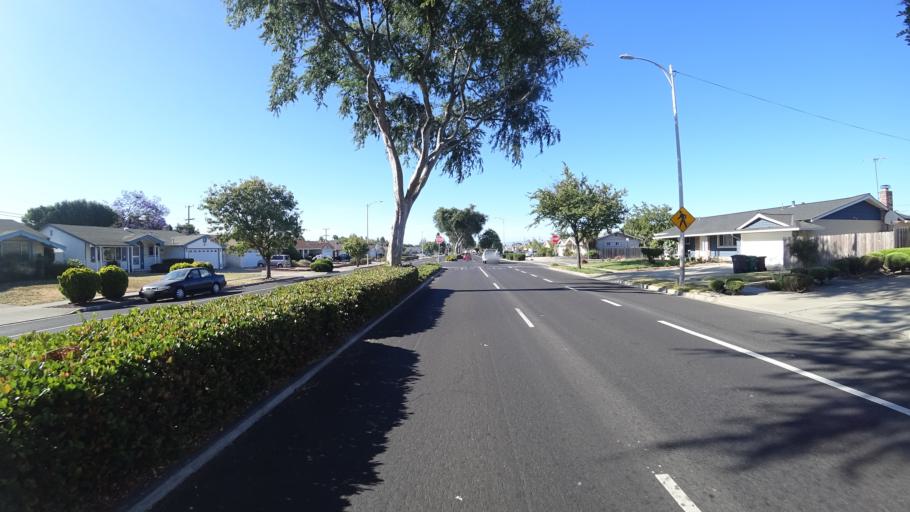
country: US
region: California
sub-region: Alameda County
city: Hayward
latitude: 37.6443
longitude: -122.0991
